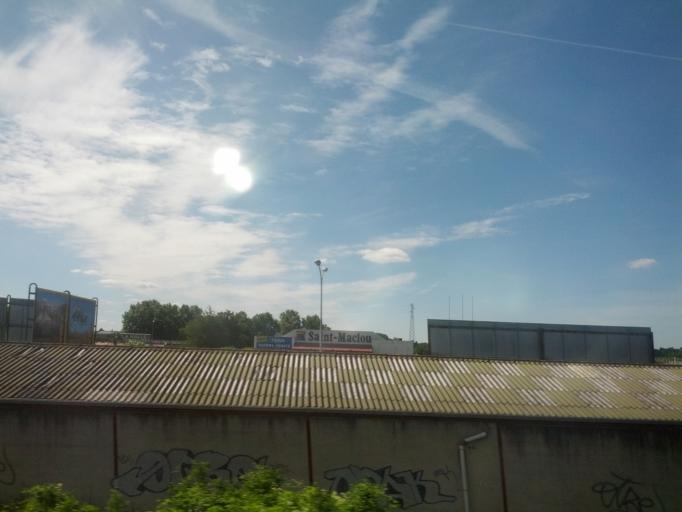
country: FR
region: Poitou-Charentes
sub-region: Departement de la Charente
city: La Couronne
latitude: 45.6221
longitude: 0.1105
